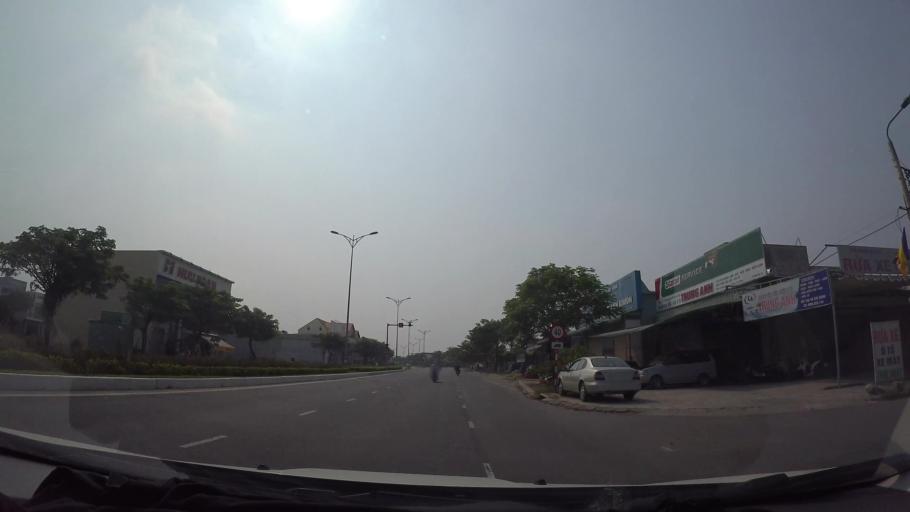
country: VN
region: Da Nang
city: Cam Le
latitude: 16.0067
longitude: 108.2204
